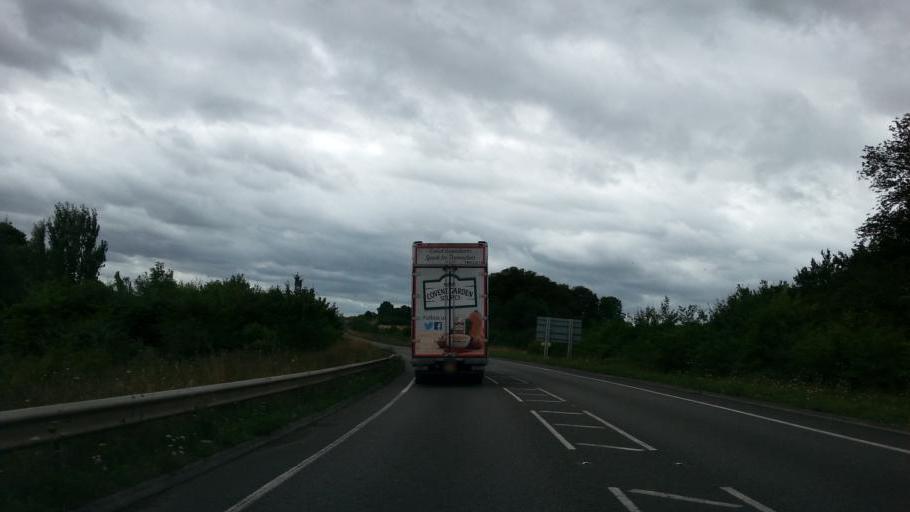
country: GB
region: England
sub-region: Cambridgeshire
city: Papworth Everard
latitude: 52.2556
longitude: -0.1250
